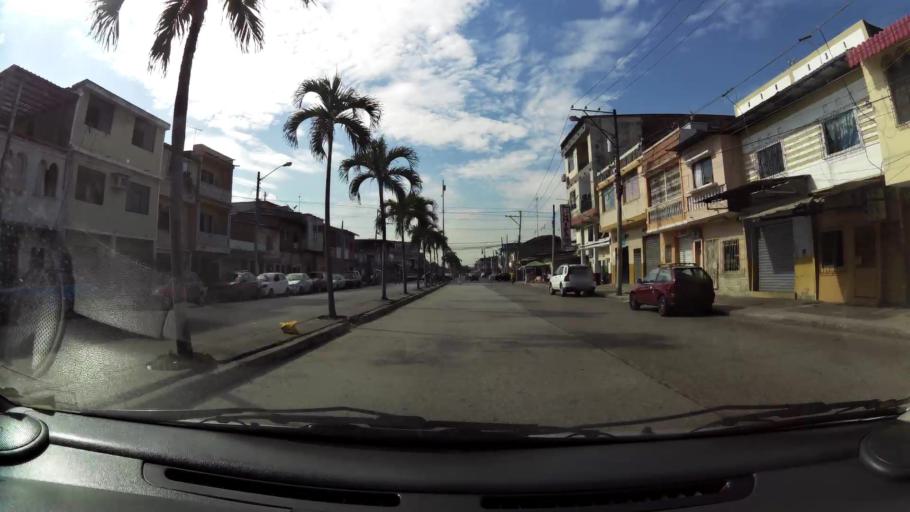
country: EC
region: Guayas
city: Guayaquil
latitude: -2.2105
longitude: -79.9122
